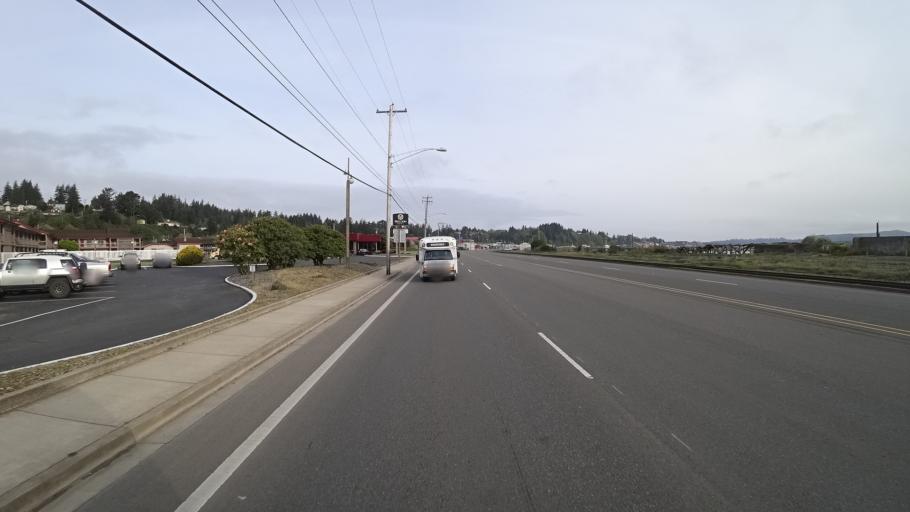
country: US
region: Oregon
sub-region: Coos County
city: Coos Bay
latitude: 43.3772
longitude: -124.2157
